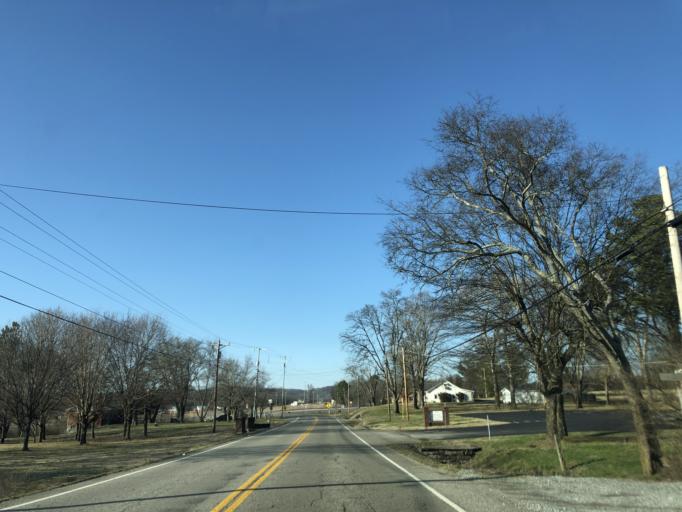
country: US
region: Tennessee
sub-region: Sumner County
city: Gallatin
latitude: 36.4259
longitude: -86.4611
